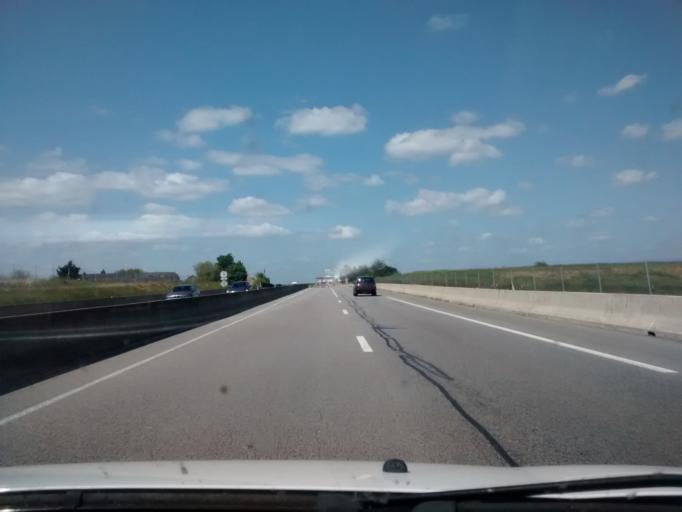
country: FR
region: Ile-de-France
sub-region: Departement des Yvelines
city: Ablis
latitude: 48.5637
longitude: 1.8324
